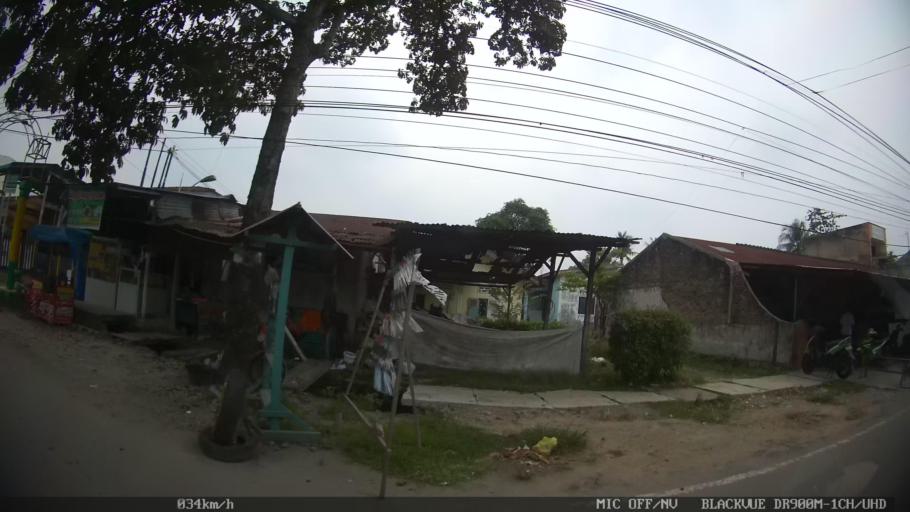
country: ID
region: North Sumatra
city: Medan
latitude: 3.5594
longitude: 98.7029
